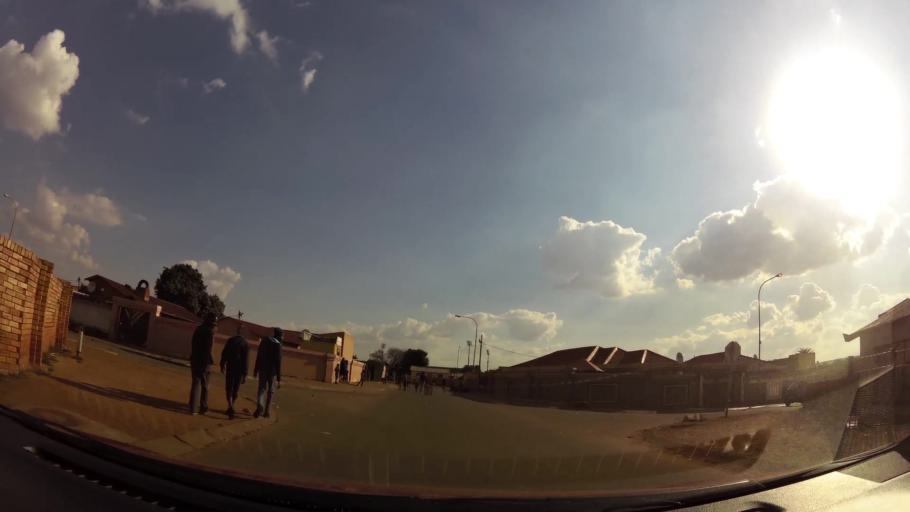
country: ZA
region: Gauteng
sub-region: City of Johannesburg Metropolitan Municipality
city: Soweto
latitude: -26.2257
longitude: 27.8700
